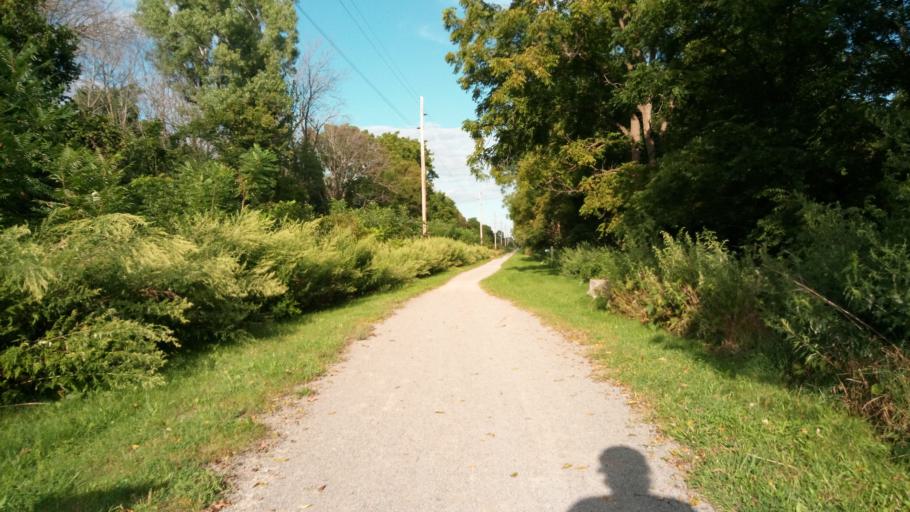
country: US
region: New York
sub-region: Monroe County
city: Pittsford
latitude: 43.0002
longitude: -77.5005
